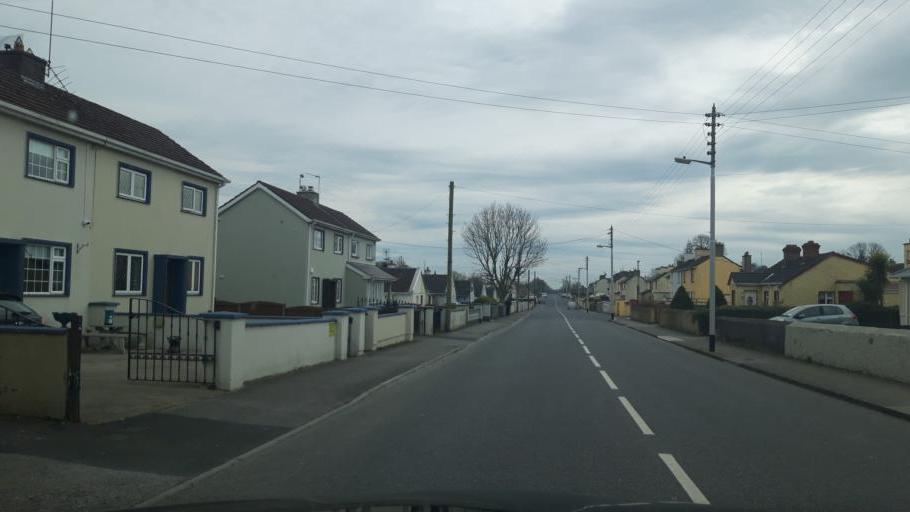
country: IE
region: Leinster
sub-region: Uibh Fhaili
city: Edenderry
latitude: 53.3418
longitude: -7.0461
